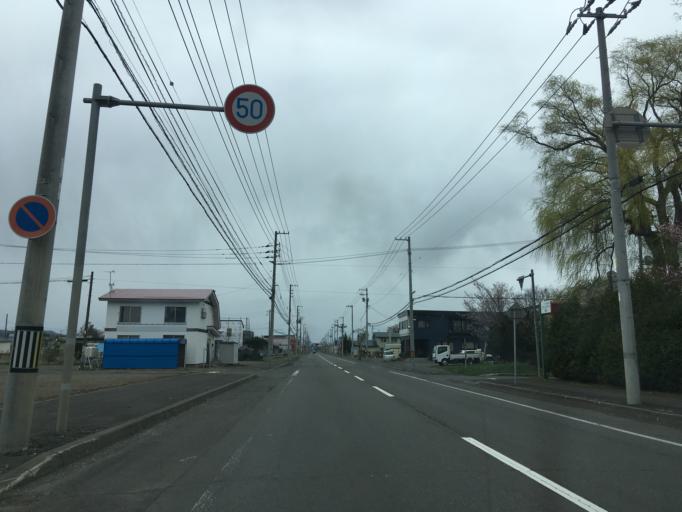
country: JP
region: Hokkaido
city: Chitose
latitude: 42.9419
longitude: 141.8044
